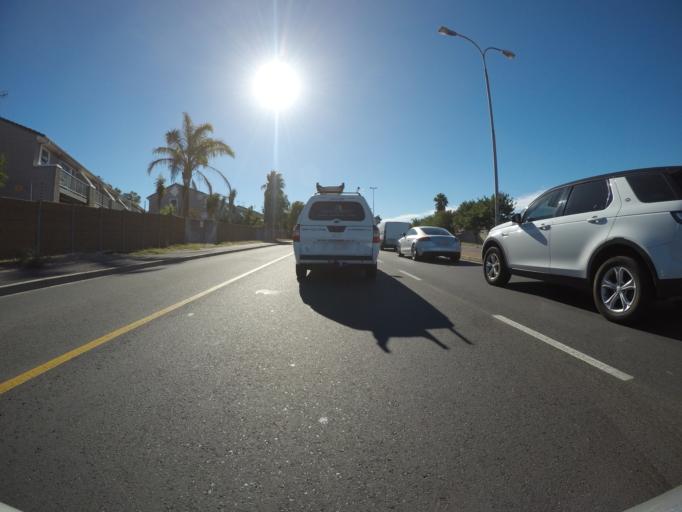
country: ZA
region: Western Cape
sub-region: City of Cape Town
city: Kraaifontein
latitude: -33.8833
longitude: 18.6660
